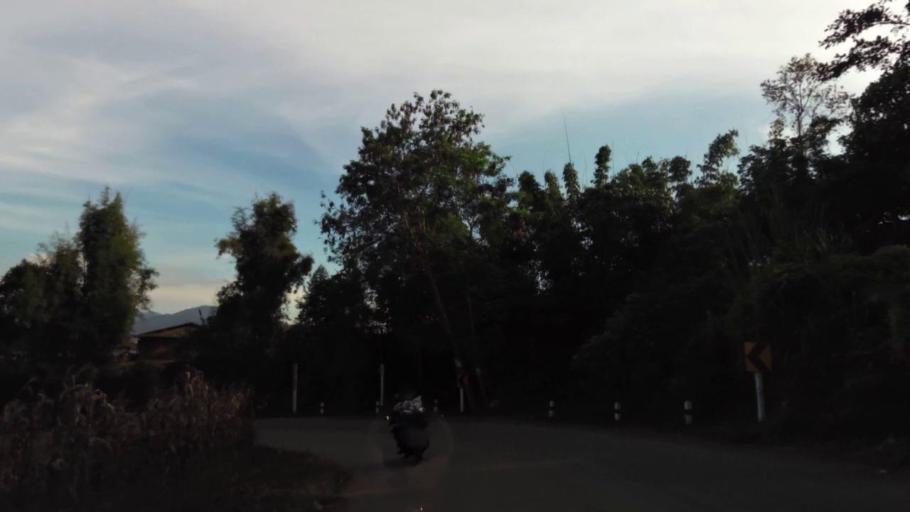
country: TH
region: Chiang Rai
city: Khun Tan
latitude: 19.8602
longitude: 100.3679
